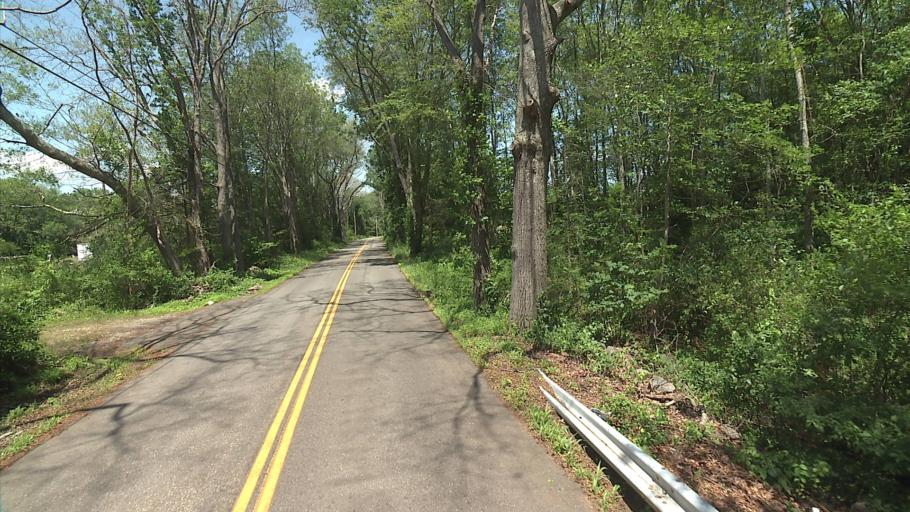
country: US
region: Connecticut
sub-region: New London County
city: Jewett City
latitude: 41.6009
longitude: -71.9067
